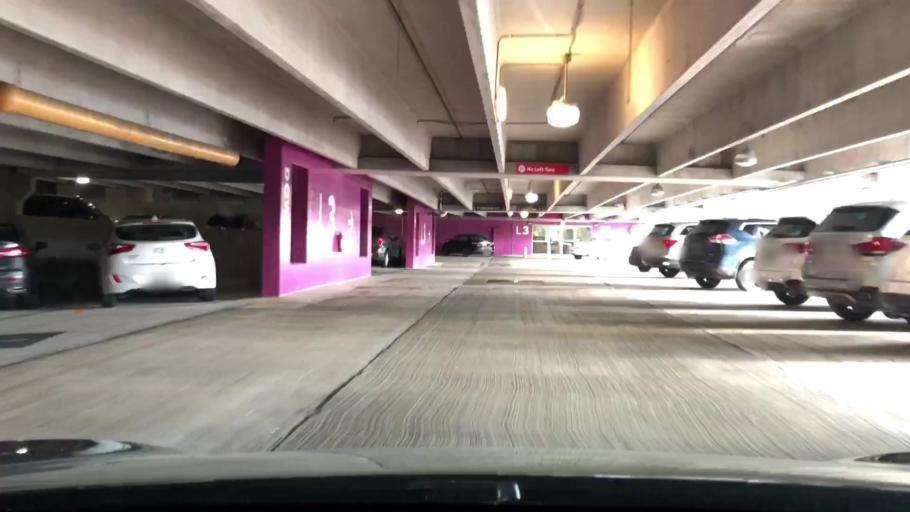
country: US
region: Pennsylvania
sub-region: Delaware County
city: Broomall
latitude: 39.9894
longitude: -75.4154
